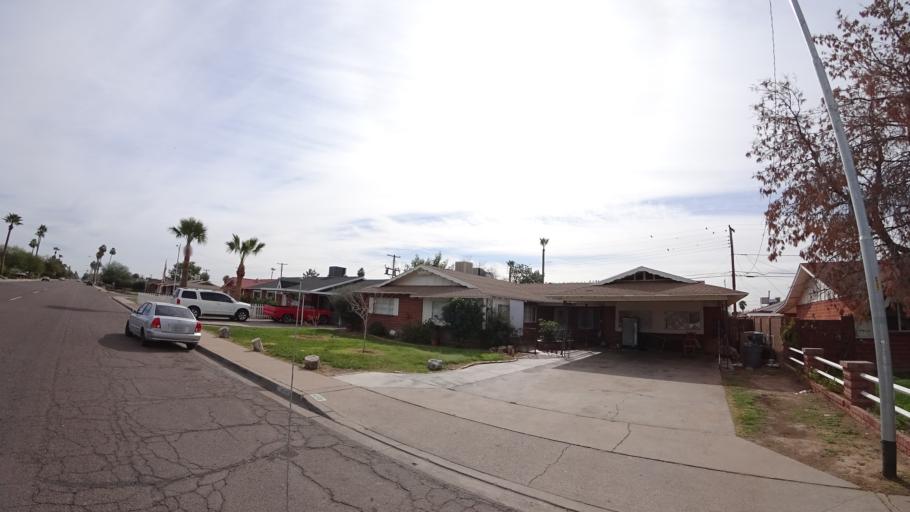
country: US
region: Arizona
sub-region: Maricopa County
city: Glendale
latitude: 33.5312
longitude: -112.1481
